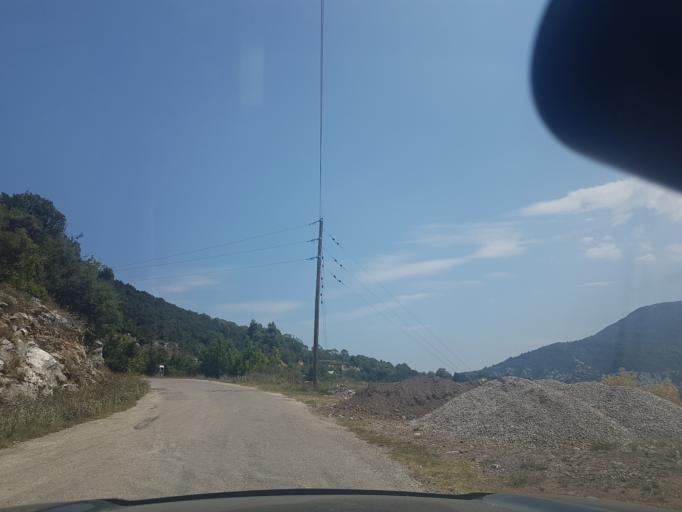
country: GR
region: Central Greece
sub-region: Nomos Evvoias
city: Yimnon
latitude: 38.6228
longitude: 23.8881
